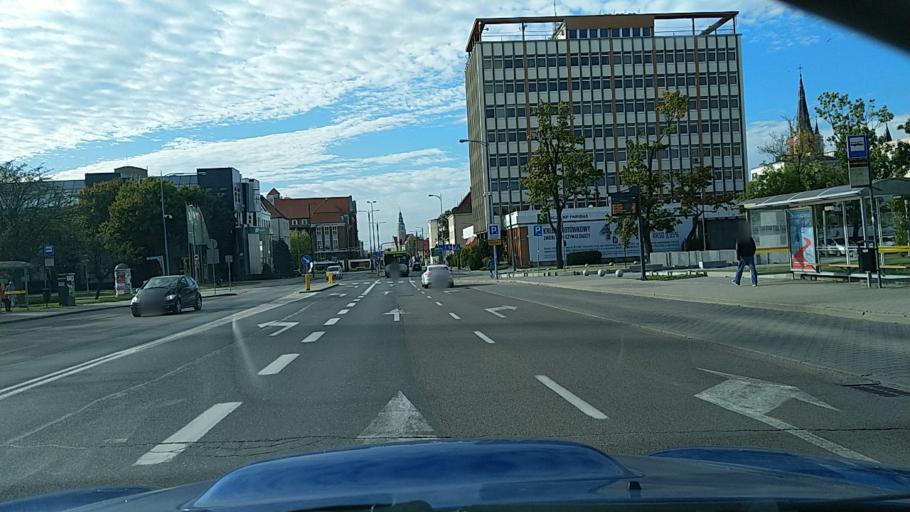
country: PL
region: Warmian-Masurian Voivodeship
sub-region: Powiat olsztynski
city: Olsztyn
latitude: 53.7758
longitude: 20.4903
